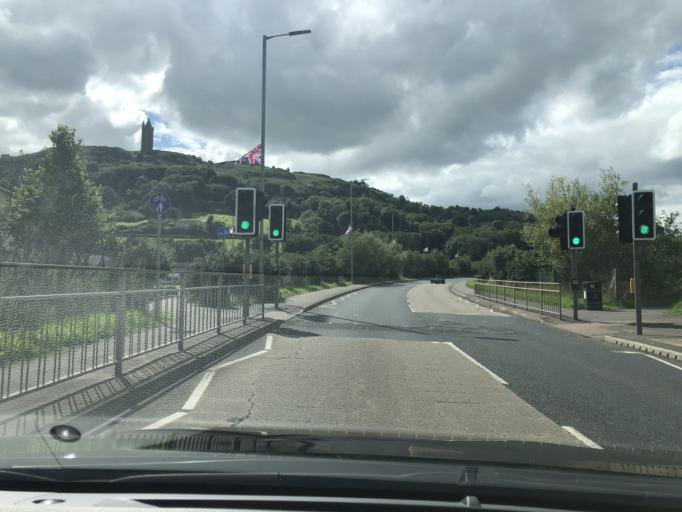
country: GB
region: Northern Ireland
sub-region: Ards District
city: Newtownards
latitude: 54.5830
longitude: -5.7057
